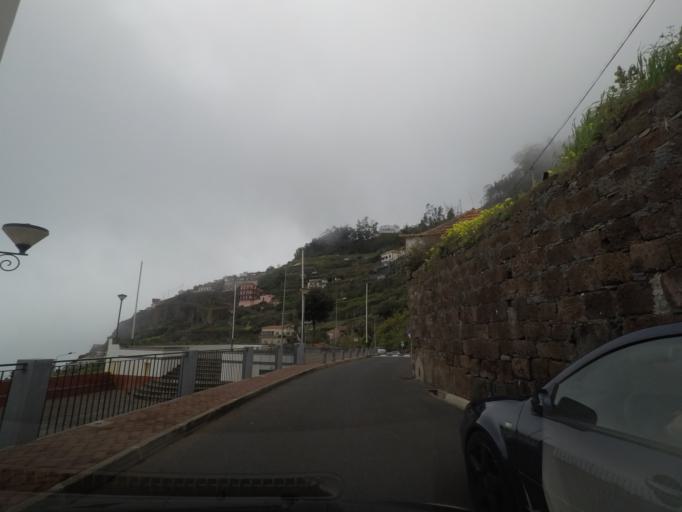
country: PT
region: Madeira
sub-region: Ribeira Brava
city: Campanario
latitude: 32.6624
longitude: -17.0116
